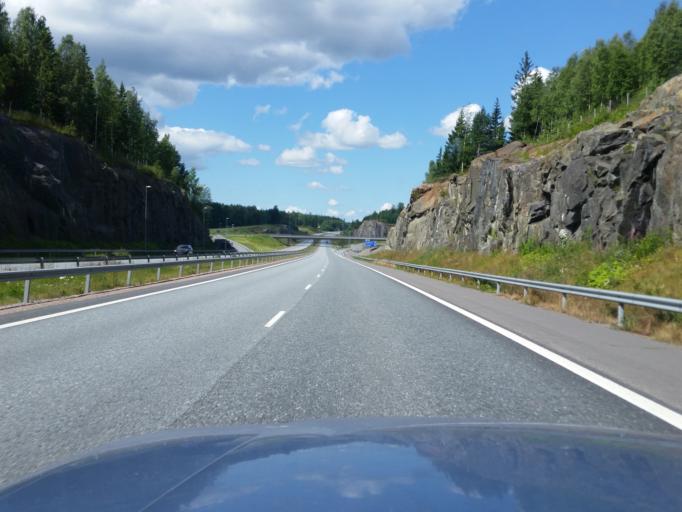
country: FI
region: Uusimaa
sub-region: Helsinki
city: Sammatti
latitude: 60.3775
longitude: 23.8154
